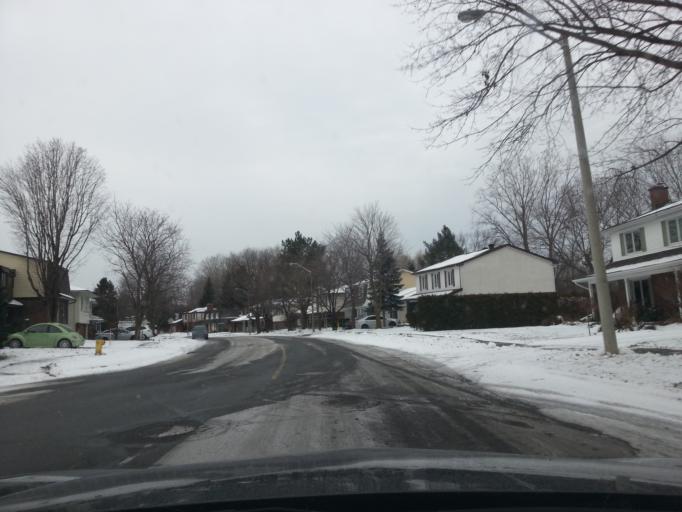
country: CA
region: Ontario
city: Ottawa
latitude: 45.3578
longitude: -75.6656
